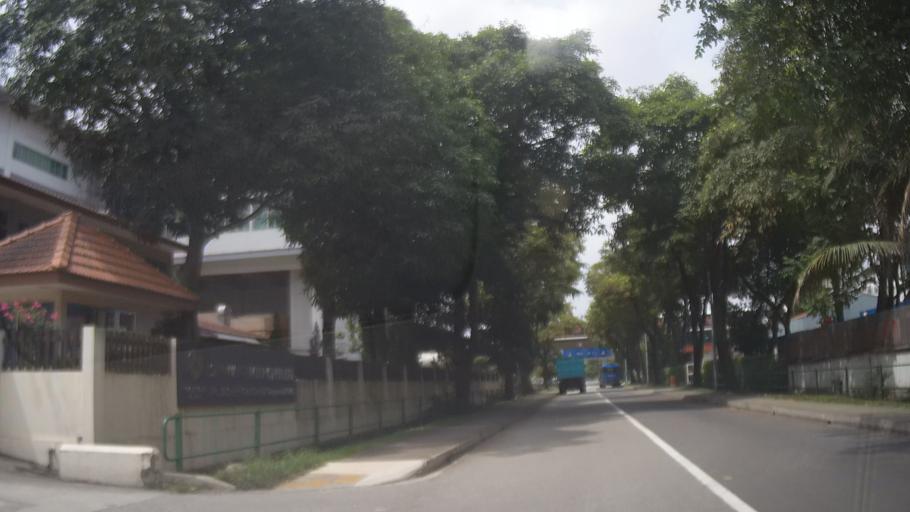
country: MY
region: Johor
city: Johor Bahru
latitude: 1.4146
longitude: 103.7502
